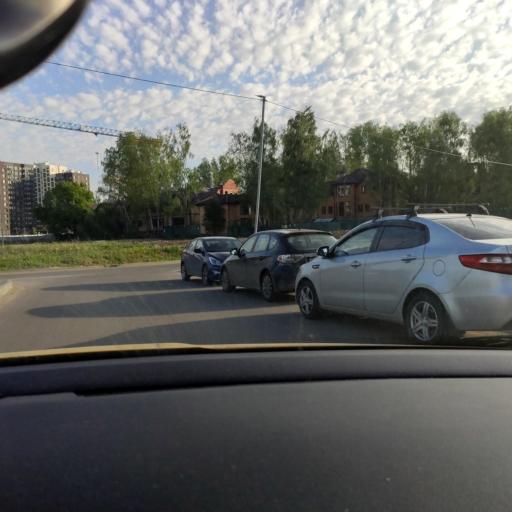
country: RU
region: Moskovskaya
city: Kommunarka
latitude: 55.5526
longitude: 37.5155
